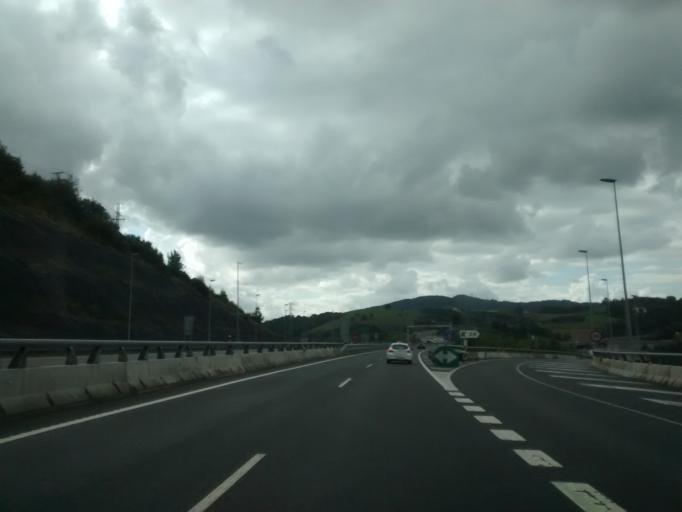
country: ES
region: Basque Country
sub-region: Provincia de Guipuzcoa
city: Lasarte
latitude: 43.2767
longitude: -2.0113
